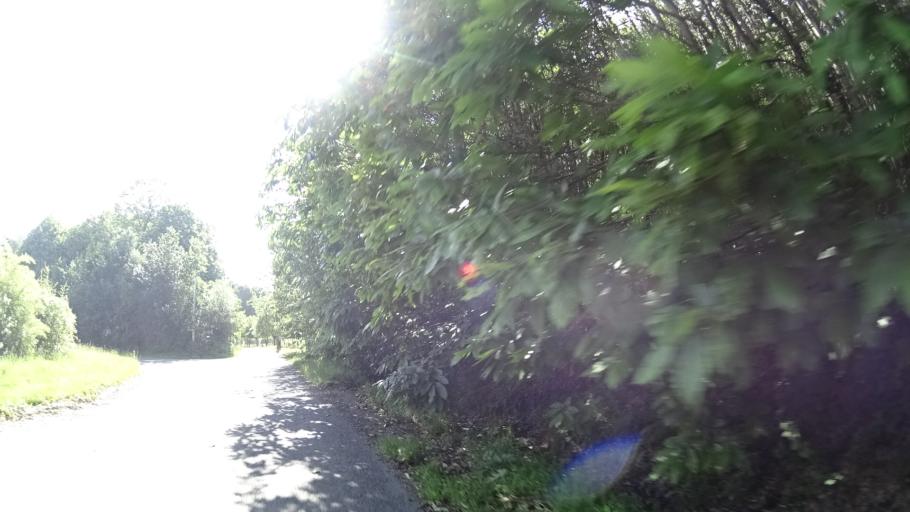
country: FR
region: Brittany
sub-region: Departement d'Ille-et-Vilaine
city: La Chapelle-des-Fougeretz
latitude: 48.1950
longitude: -1.7175
